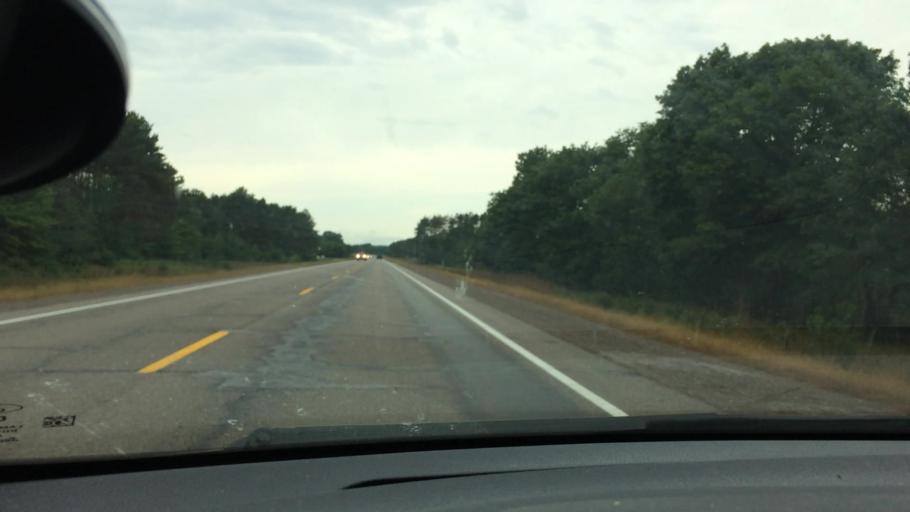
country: US
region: Wisconsin
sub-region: Eau Claire County
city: Augusta
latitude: 44.5823
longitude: -91.0857
